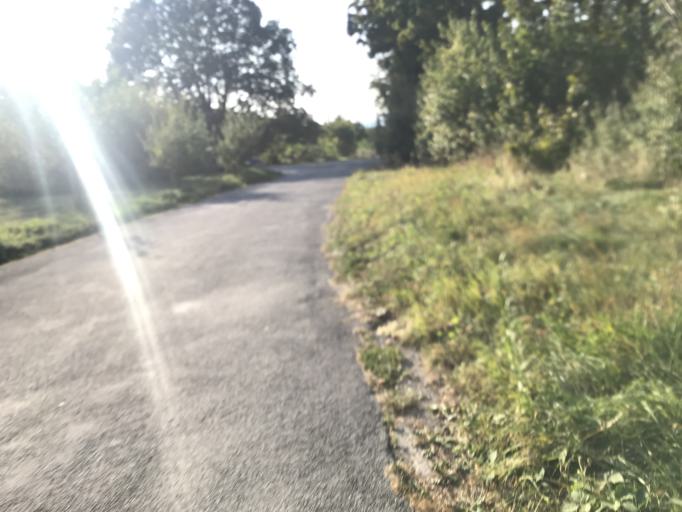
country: DE
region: Hesse
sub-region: Regierungsbezirk Kassel
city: Eschwege
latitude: 51.1911
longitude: 10.0354
